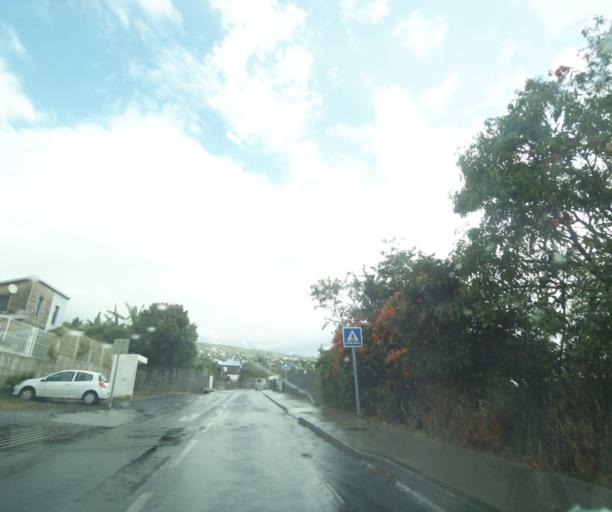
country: RE
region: Reunion
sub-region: Reunion
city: La Possession
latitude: -20.9805
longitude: 55.3285
